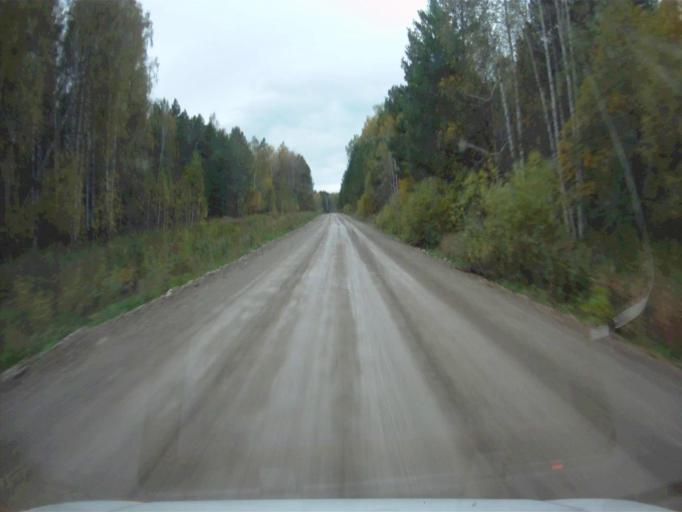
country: RU
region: Chelyabinsk
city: Nyazepetrovsk
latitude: 56.0938
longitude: 59.4060
